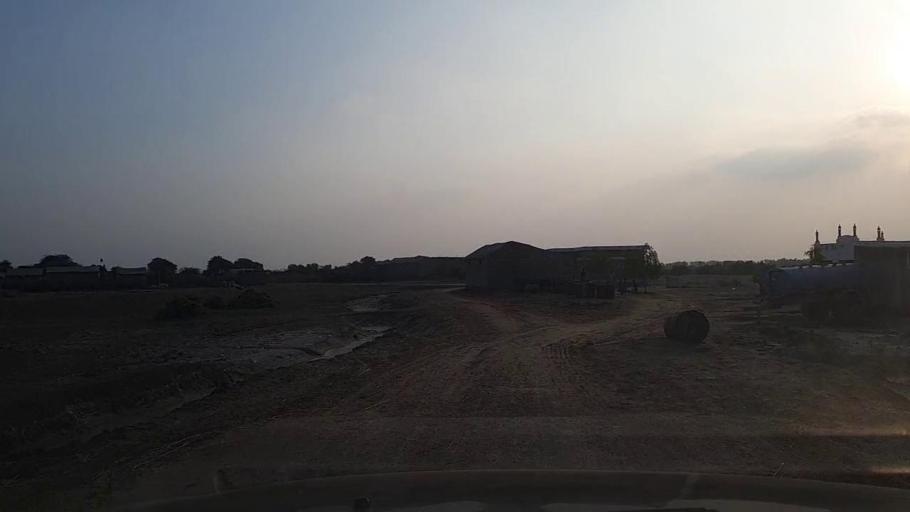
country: PK
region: Sindh
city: Jati
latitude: 24.5324
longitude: 68.3571
